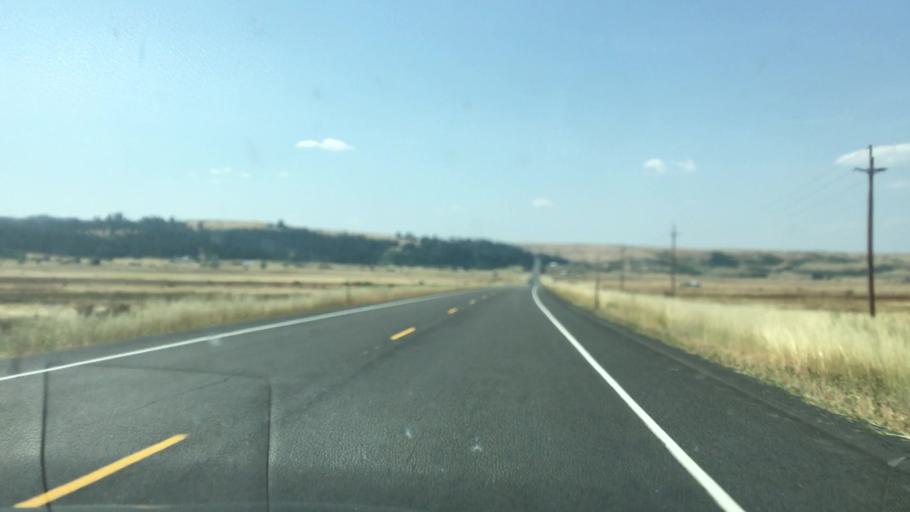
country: US
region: Idaho
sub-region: Idaho County
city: Grangeville
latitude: 45.8885
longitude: -116.2008
